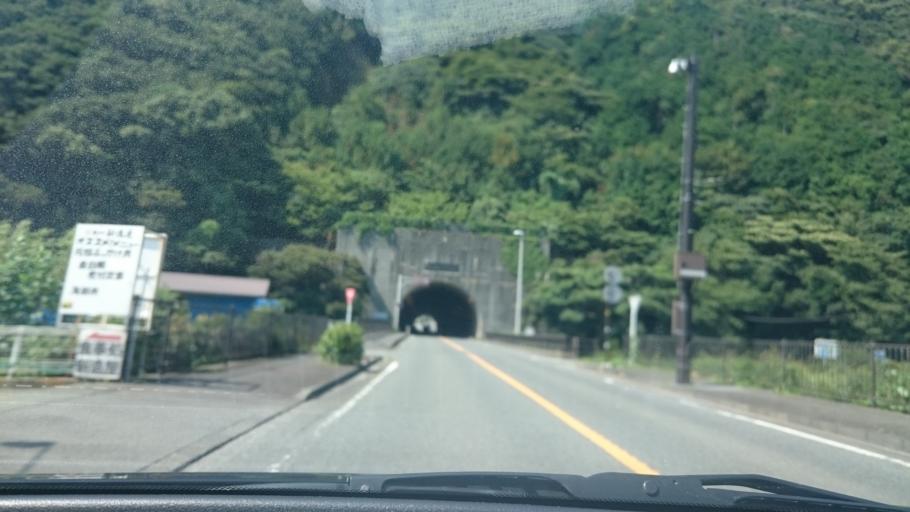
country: JP
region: Shizuoka
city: Heda
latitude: 34.8507
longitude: 138.7770
